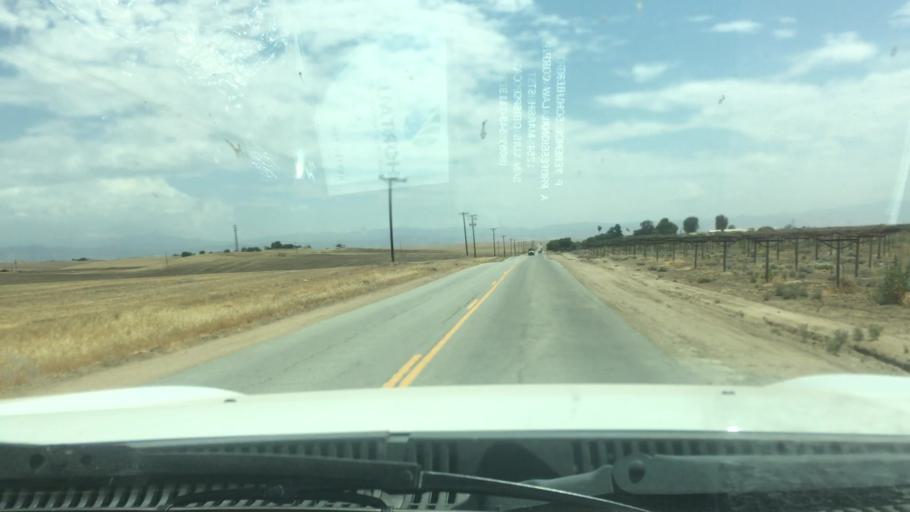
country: US
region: California
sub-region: Kern County
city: McFarland
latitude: 35.6025
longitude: -119.0987
